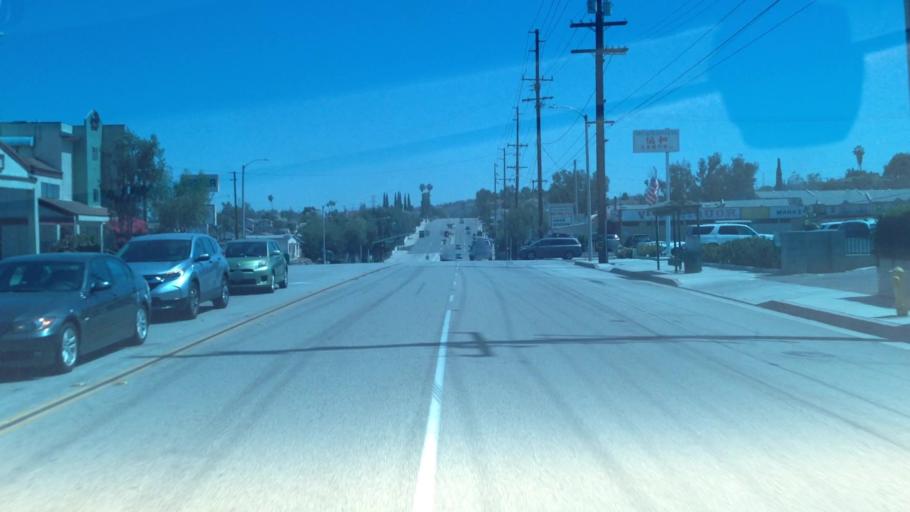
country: US
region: California
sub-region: Los Angeles County
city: South San Gabriel
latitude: 34.0537
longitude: -118.0906
